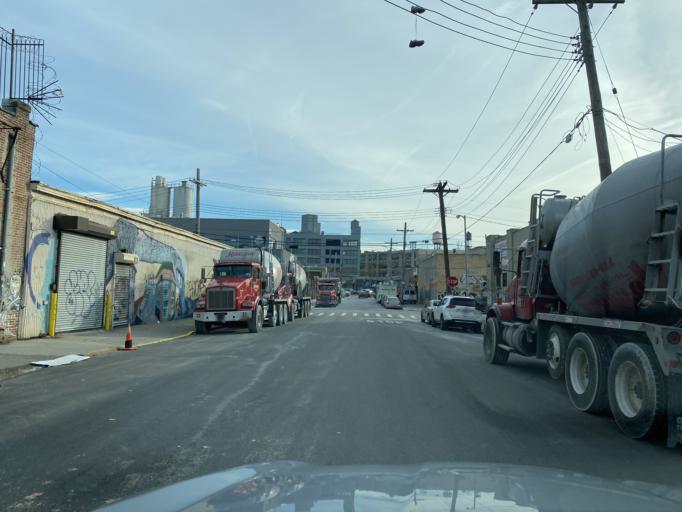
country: US
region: New York
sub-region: Queens County
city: Long Island City
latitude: 40.7083
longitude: -73.9245
